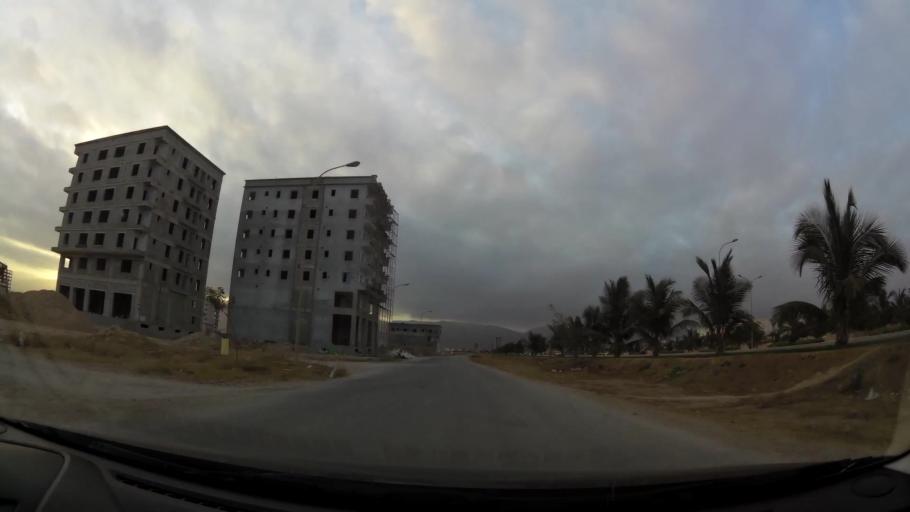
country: OM
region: Zufar
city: Salalah
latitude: 17.0255
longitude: 54.0319
